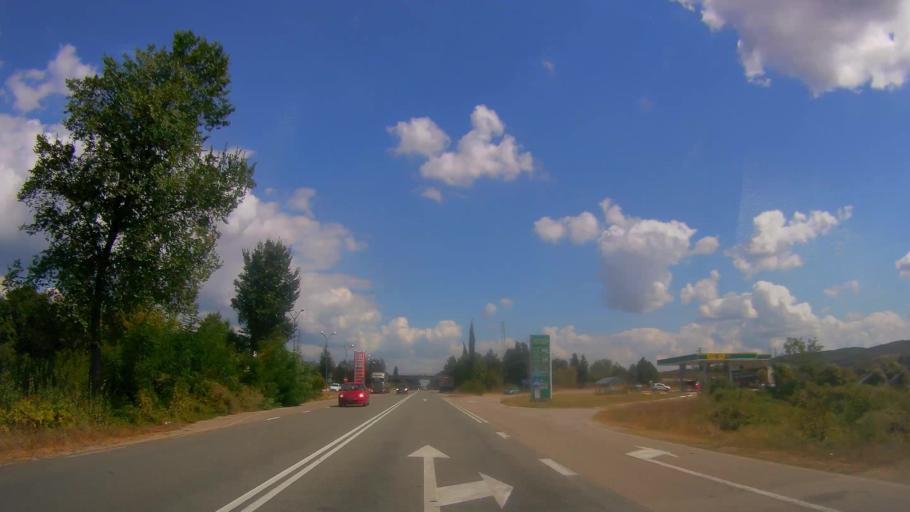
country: BG
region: Sliven
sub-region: Obshtina Tvurditsa
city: Tvurditsa
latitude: 42.6564
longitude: 25.8923
